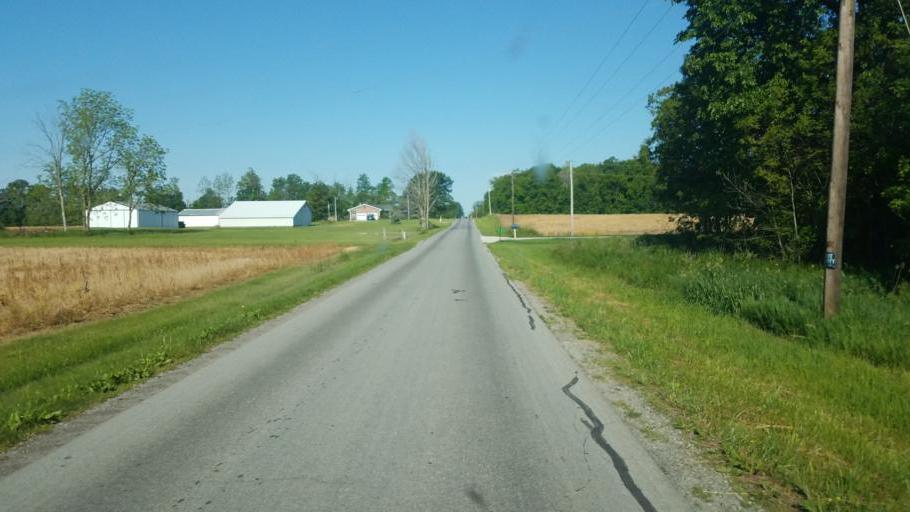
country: US
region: Ohio
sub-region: Hardin County
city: Kenton
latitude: 40.5795
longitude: -83.5645
